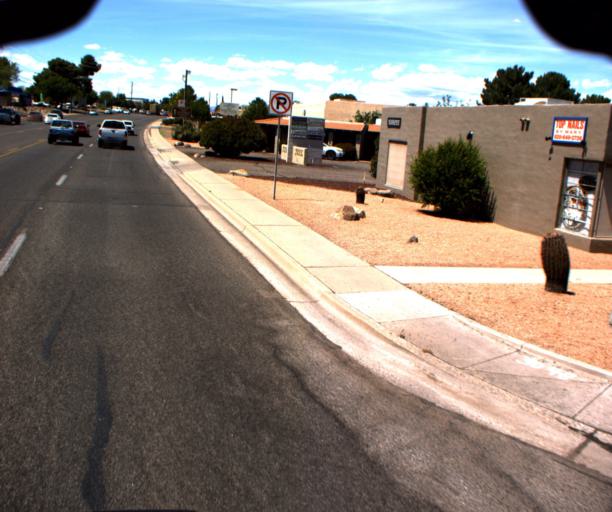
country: US
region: Arizona
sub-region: Yavapai County
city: Cottonwood
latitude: 34.7261
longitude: -112.0079
